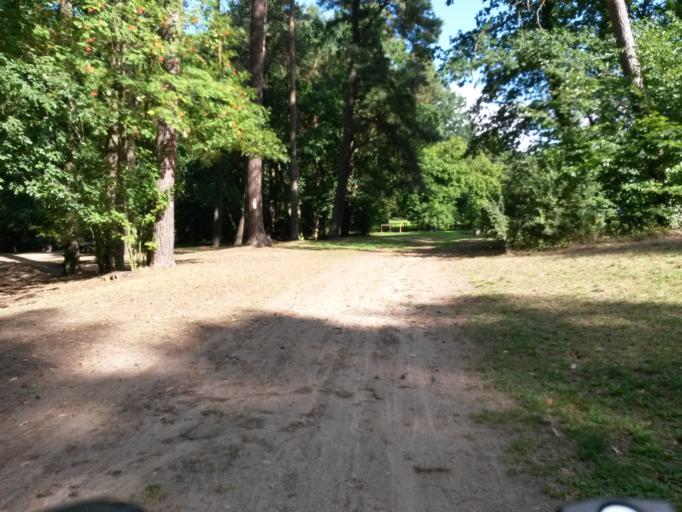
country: DE
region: Brandenburg
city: Templin
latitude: 53.2151
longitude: 13.5152
